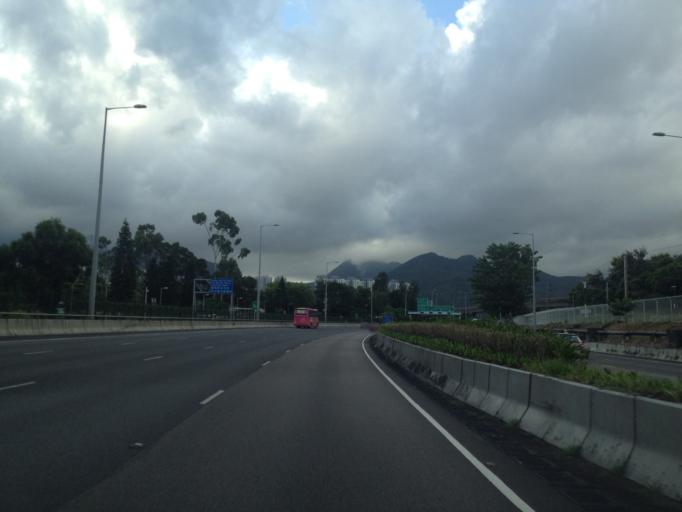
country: HK
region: Sha Tin
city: Sha Tin
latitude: 22.4227
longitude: 114.2127
